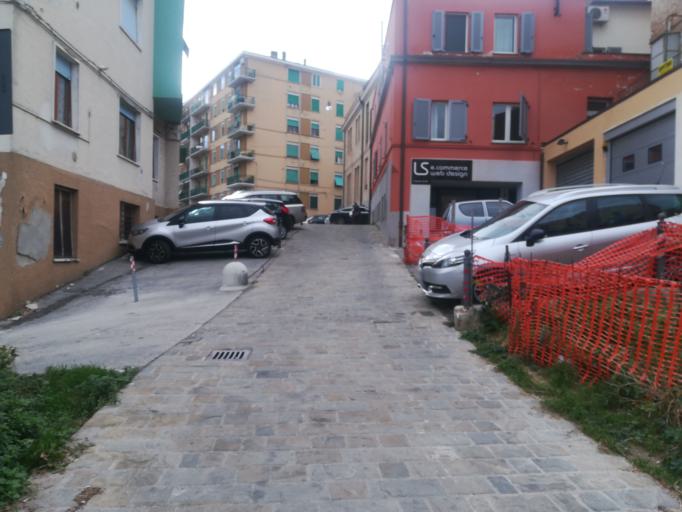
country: IT
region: The Marches
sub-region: Provincia di Macerata
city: Macerata
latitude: 43.2973
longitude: 13.4565
